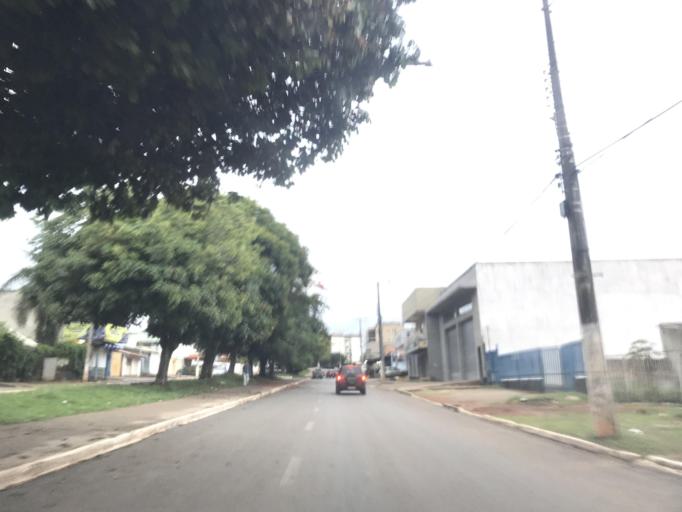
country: BR
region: Goias
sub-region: Luziania
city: Luziania
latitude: -16.2609
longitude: -47.9578
